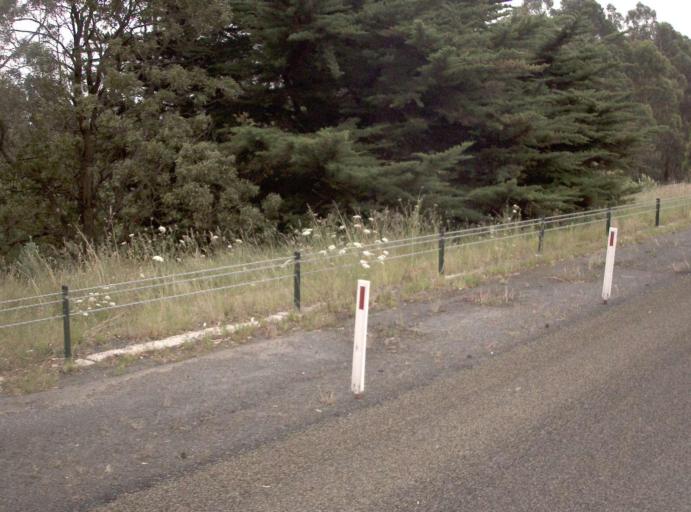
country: AU
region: Victoria
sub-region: Baw Baw
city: Warragul
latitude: -38.1408
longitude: 145.8838
